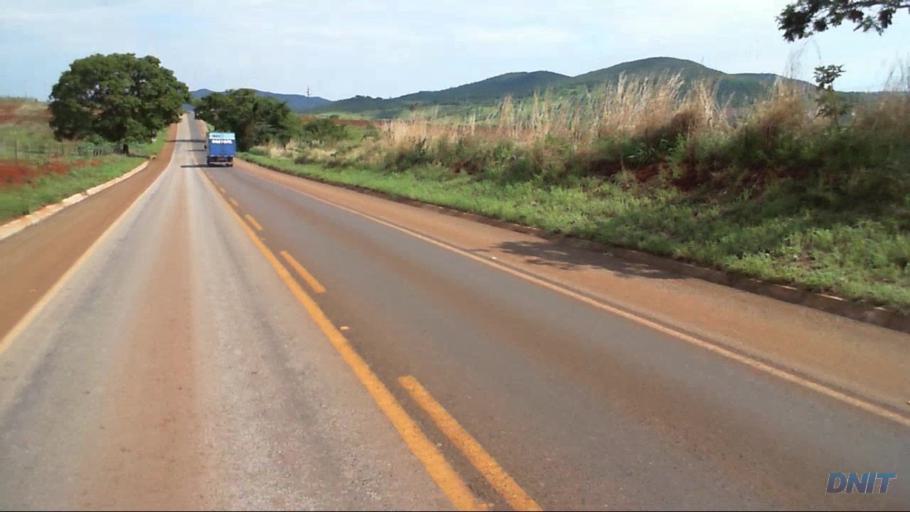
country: BR
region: Goias
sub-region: Barro Alto
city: Barro Alto
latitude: -14.9988
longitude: -48.9055
